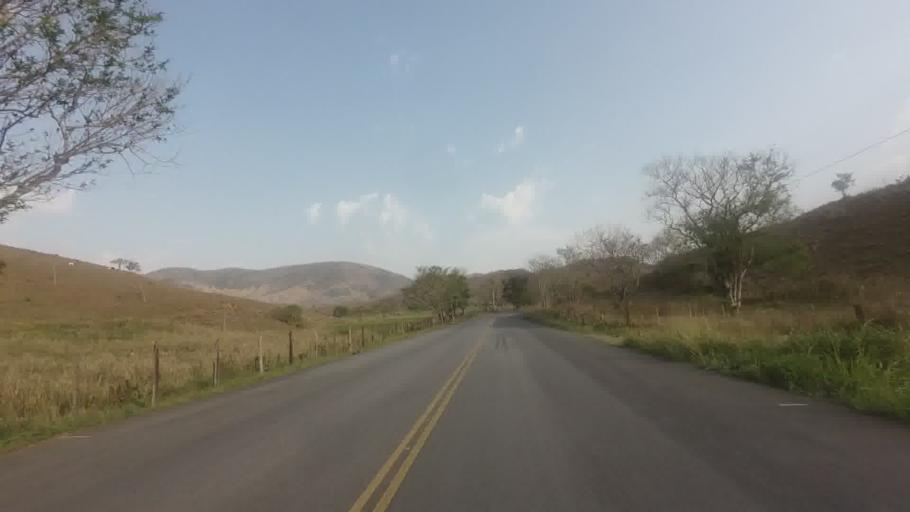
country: BR
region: Rio de Janeiro
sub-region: Cambuci
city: Cambuci
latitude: -21.4009
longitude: -41.9759
